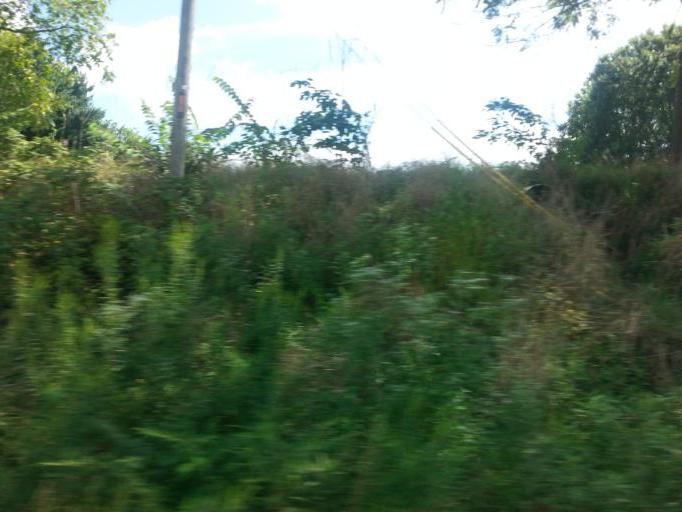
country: US
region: Virginia
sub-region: Washington County
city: Abingdon
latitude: 36.6682
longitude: -82.0604
